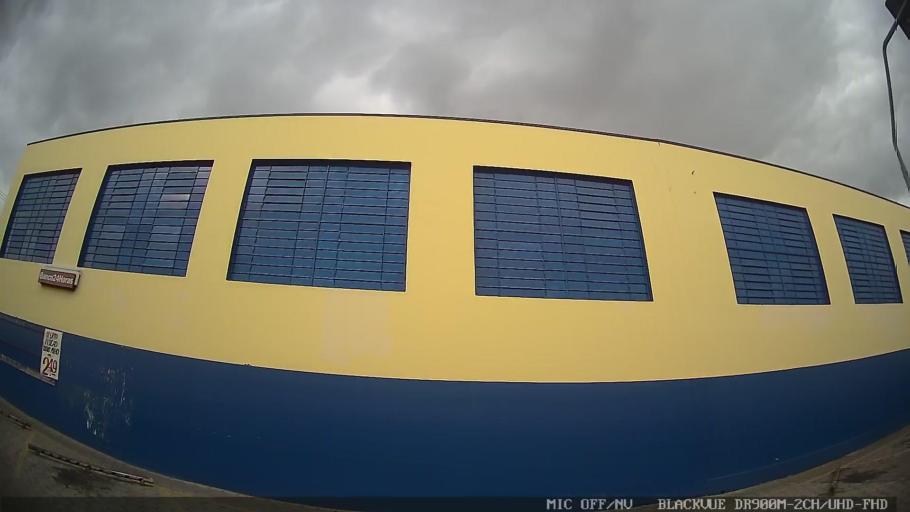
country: BR
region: Sao Paulo
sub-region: Indaiatuba
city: Indaiatuba
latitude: -23.1096
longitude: -47.2389
